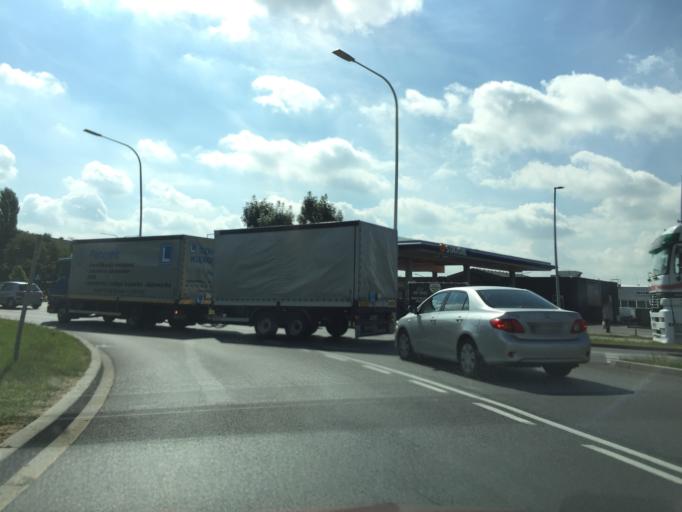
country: PL
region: Greater Poland Voivodeship
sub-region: Kalisz
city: Kalisz
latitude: 51.7485
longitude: 18.0632
